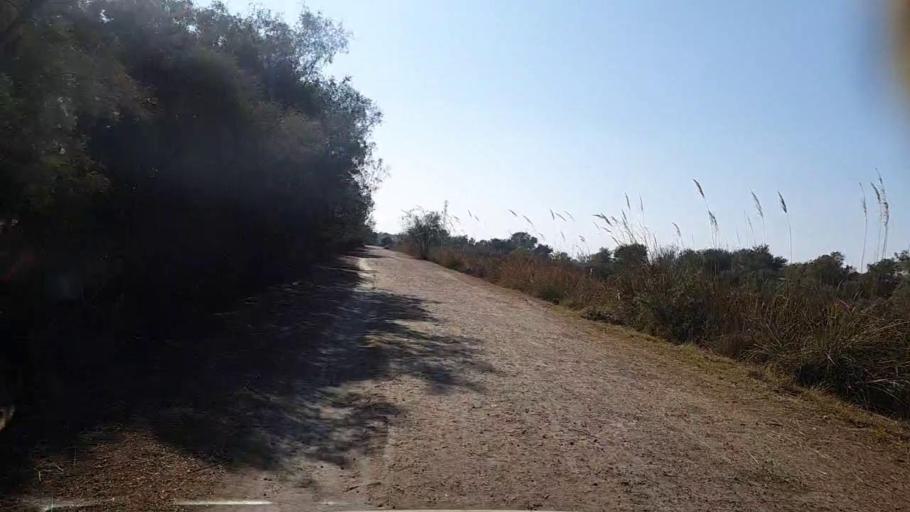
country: PK
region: Sindh
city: Khairpur
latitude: 27.9417
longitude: 69.7244
